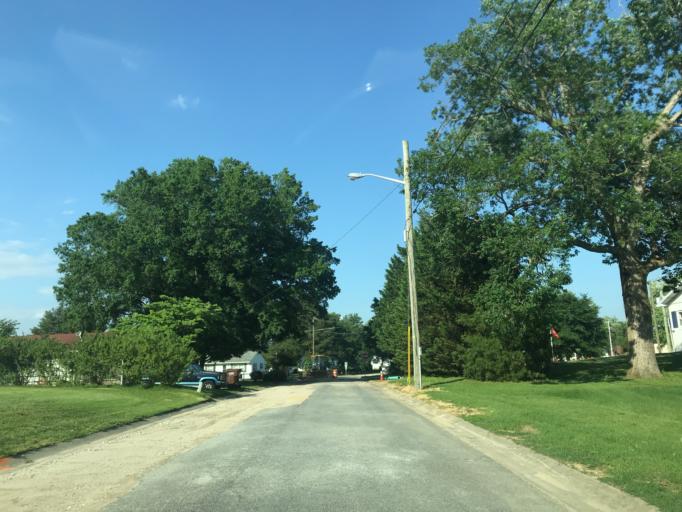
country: US
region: Maryland
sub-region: Wicomico County
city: Hebron
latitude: 38.5394
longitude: -75.7159
